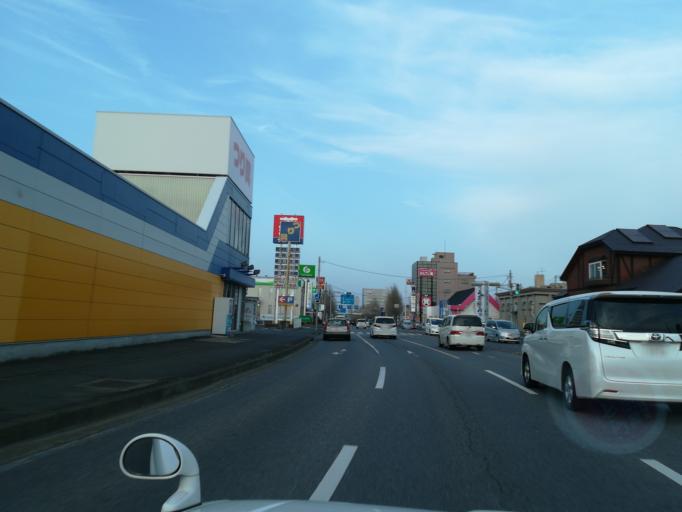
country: JP
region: Ibaraki
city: Naka
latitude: 36.0718
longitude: 140.0944
